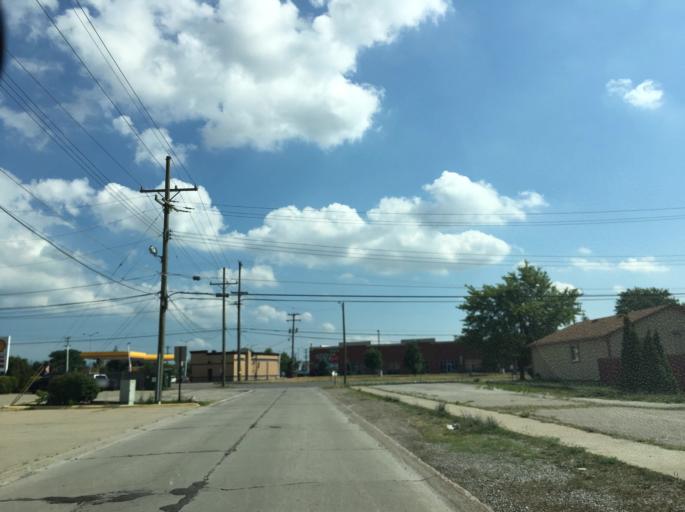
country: US
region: Michigan
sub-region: Macomb County
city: Fraser
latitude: 42.5404
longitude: -82.9101
